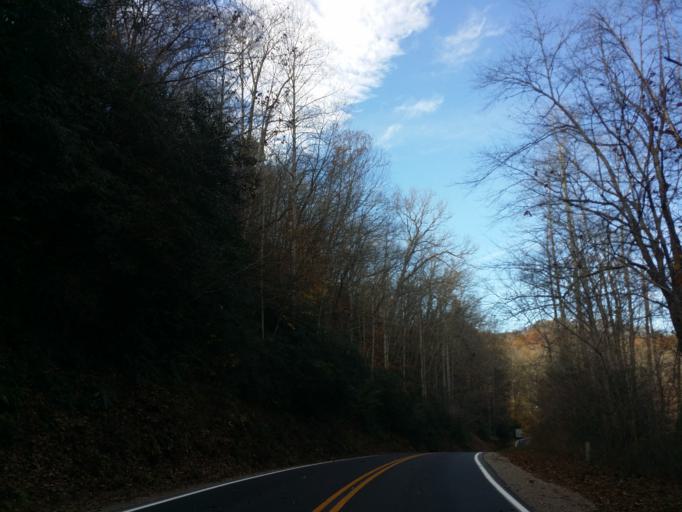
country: US
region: North Carolina
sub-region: McDowell County
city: Marion
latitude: 35.7229
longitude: -82.0867
